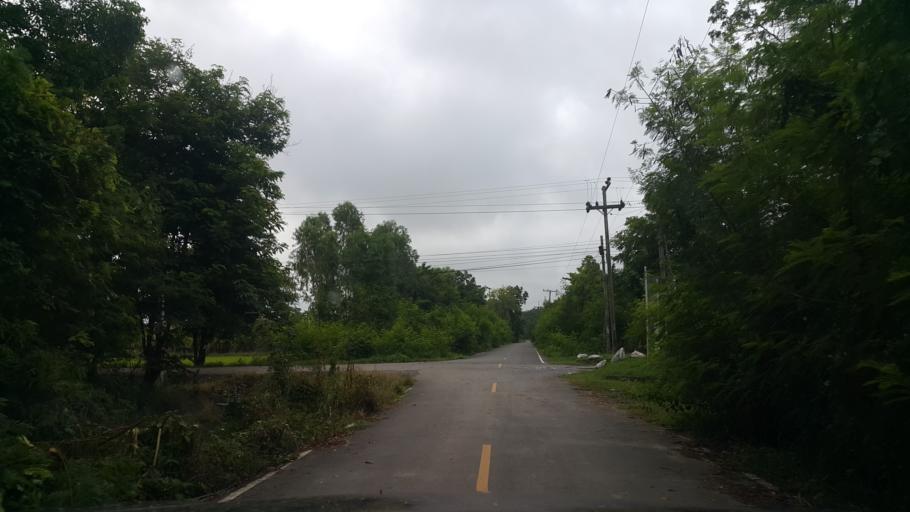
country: TH
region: Sukhothai
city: Sawankhalok
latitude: 17.3074
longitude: 99.7071
